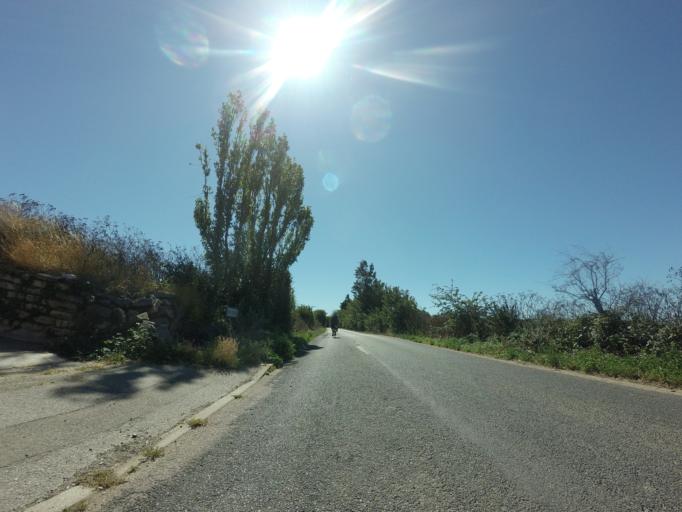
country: GB
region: England
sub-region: Kent
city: Ash
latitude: 51.2737
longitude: 1.2931
